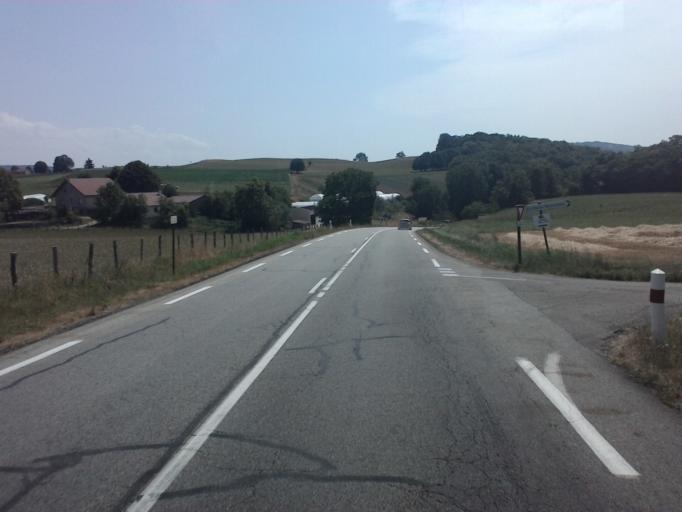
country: FR
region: Rhone-Alpes
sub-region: Departement de l'Isere
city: Bilieu
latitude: 45.4575
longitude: 5.5750
